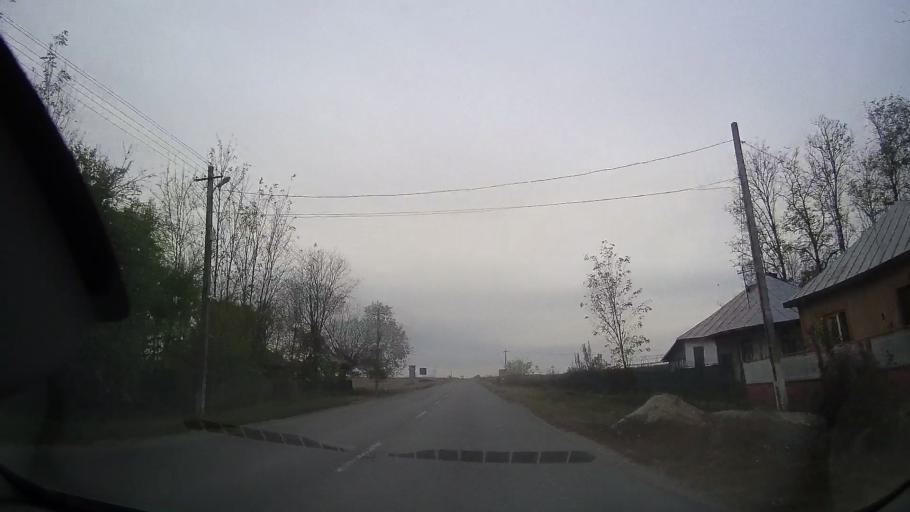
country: RO
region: Ialomita
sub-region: Comuna Grivita
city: Grivita
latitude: 44.7401
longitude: 27.2799
